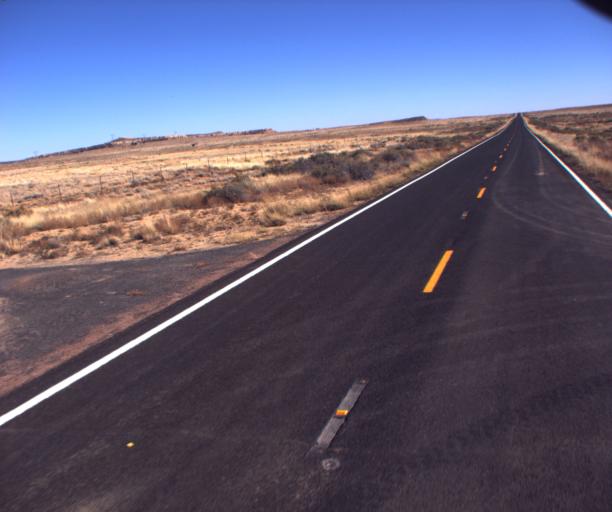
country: US
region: Arizona
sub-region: Navajo County
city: First Mesa
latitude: 35.9731
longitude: -110.7774
